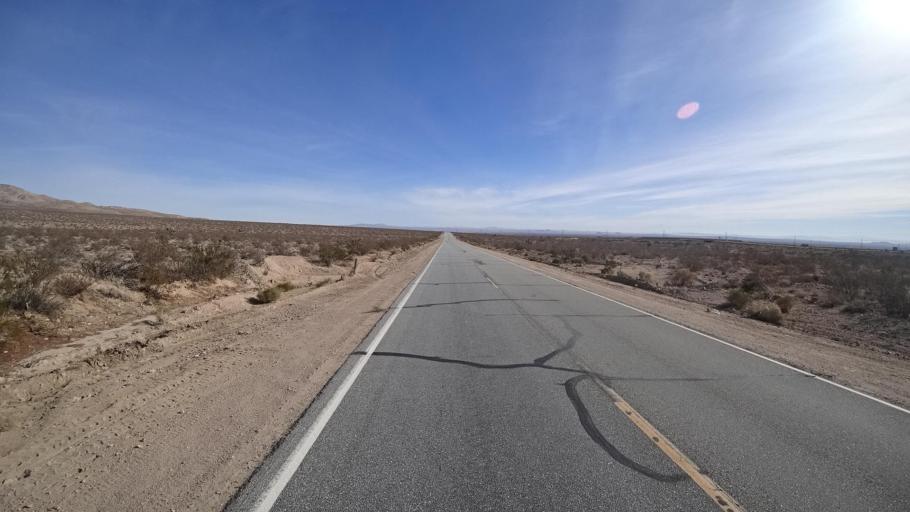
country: US
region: California
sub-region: Kern County
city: Mojave
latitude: 35.1193
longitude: -118.1958
